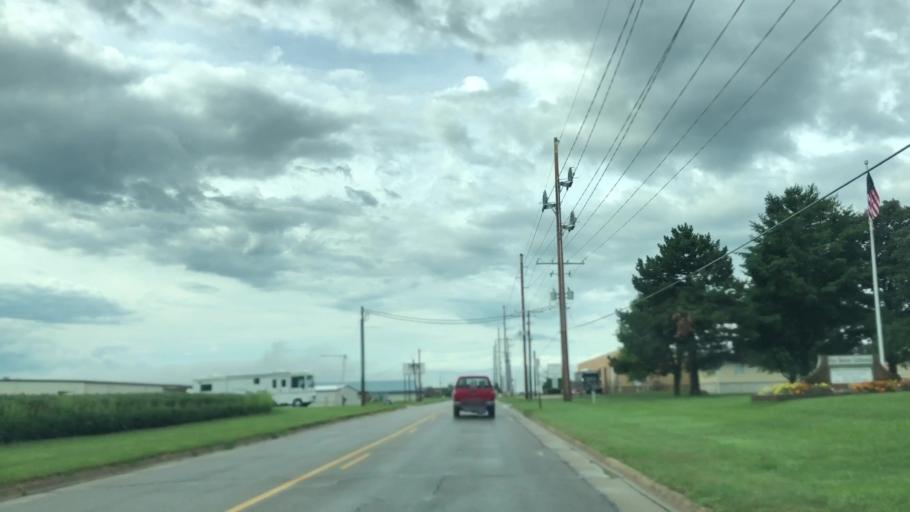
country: US
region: Iowa
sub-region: Marshall County
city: Marshalltown
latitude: 42.0102
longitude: -92.9222
